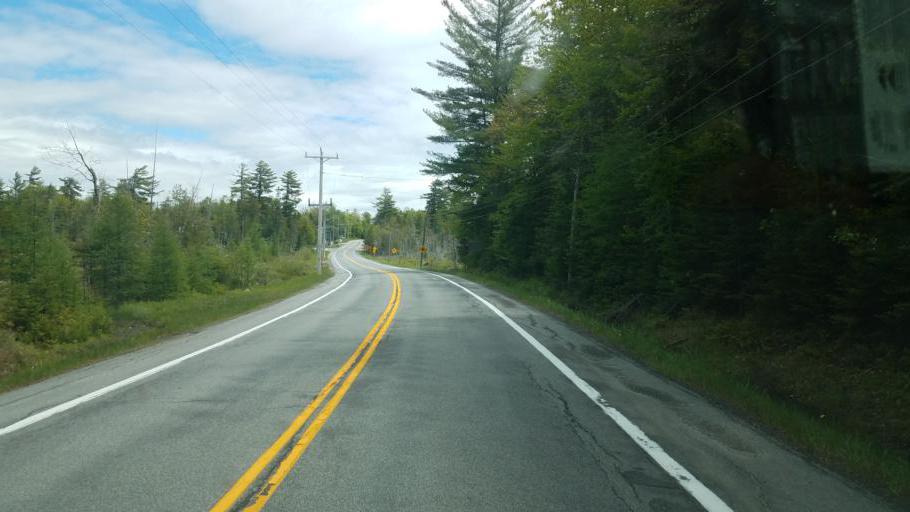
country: US
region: New York
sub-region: Hamilton County
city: Lake Pleasant
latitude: 43.8069
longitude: -74.6580
